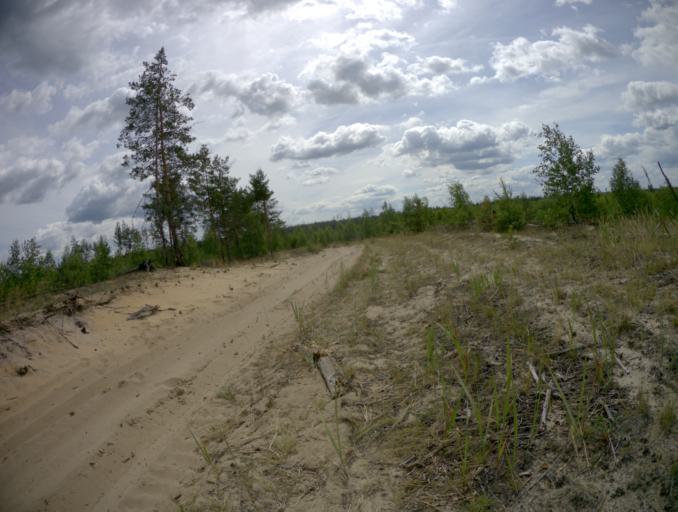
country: RU
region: Nizjnij Novgorod
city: Frolishchi
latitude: 56.5024
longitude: 42.5362
